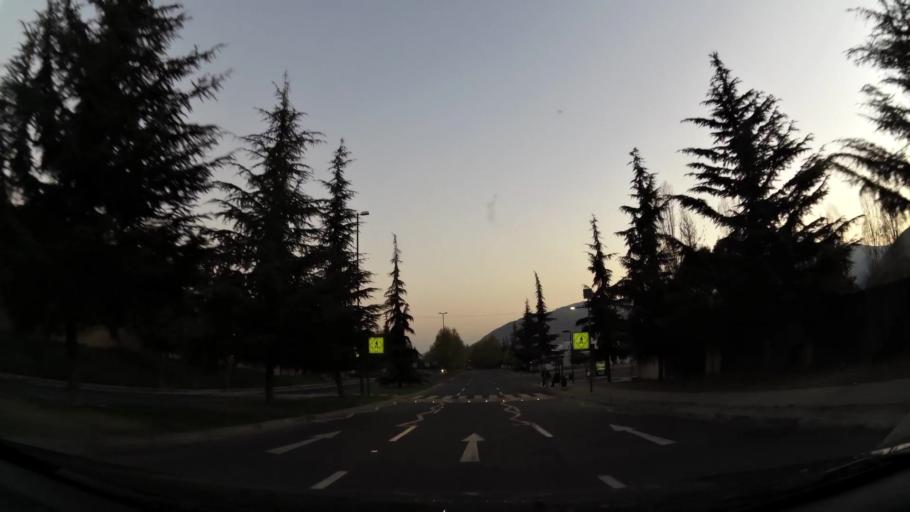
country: CL
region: Santiago Metropolitan
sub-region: Provincia de Chacabuco
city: Chicureo Abajo
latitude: -33.3261
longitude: -70.5424
